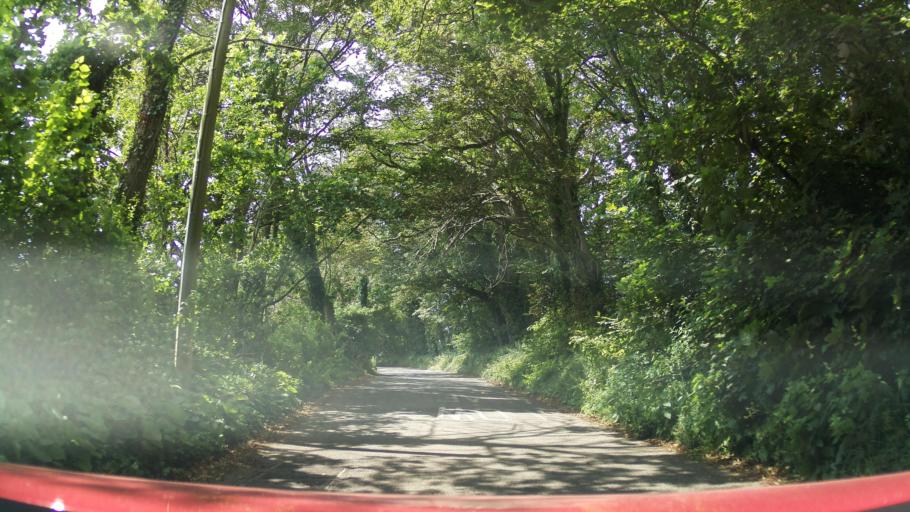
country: GB
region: Wales
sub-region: Vale of Glamorgan
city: Llantwit Major
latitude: 51.4071
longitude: -3.4978
